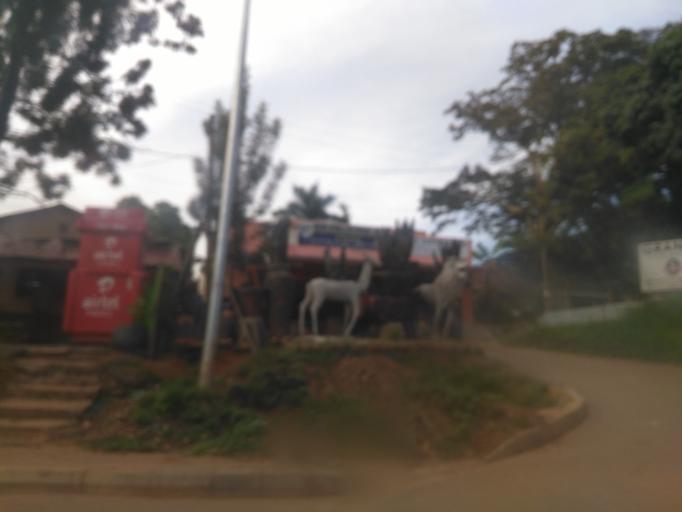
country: UG
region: Central Region
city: Kampala Central Division
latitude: 0.3475
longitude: 32.5973
